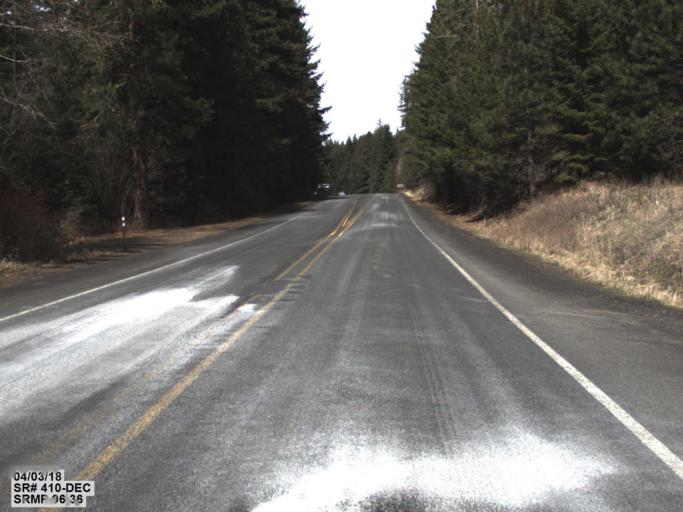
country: US
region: Washington
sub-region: Kittitas County
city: Cle Elum
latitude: 46.9392
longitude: -121.0614
